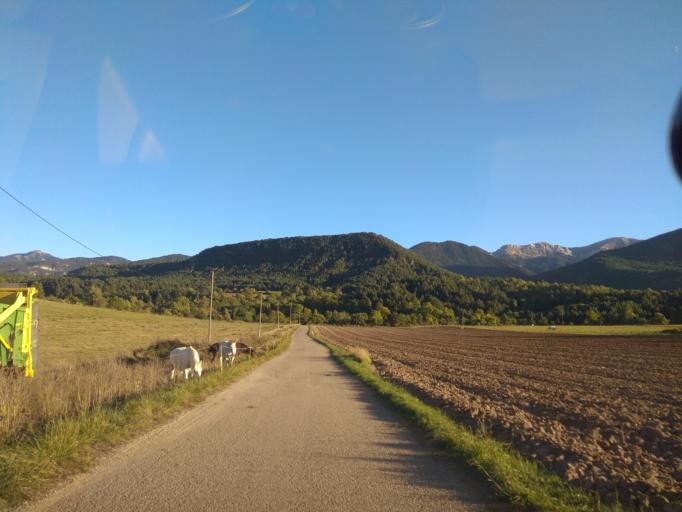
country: ES
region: Catalonia
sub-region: Provincia de Lleida
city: Lles de Cerdanya
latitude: 42.3613
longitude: 1.7275
